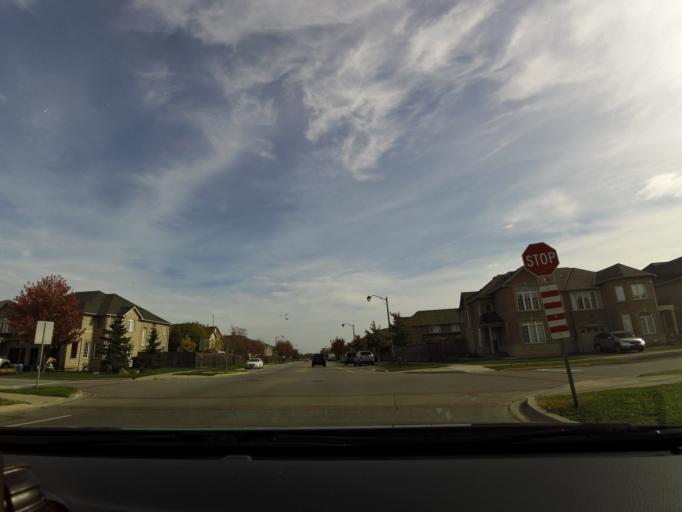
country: CA
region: Ontario
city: Burlington
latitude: 43.4105
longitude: -79.7985
